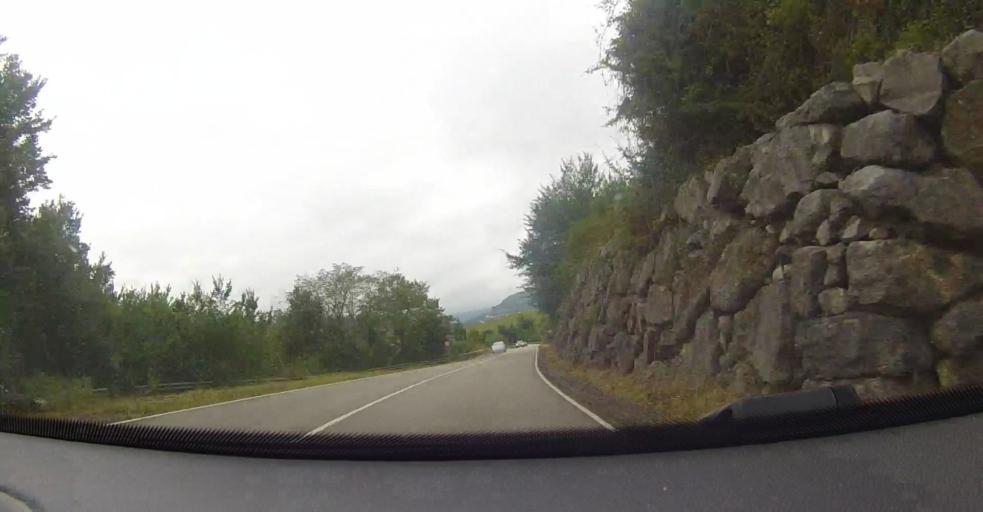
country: ES
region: Asturias
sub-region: Province of Asturias
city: Villaviciosa
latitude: 43.4891
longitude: -5.4383
